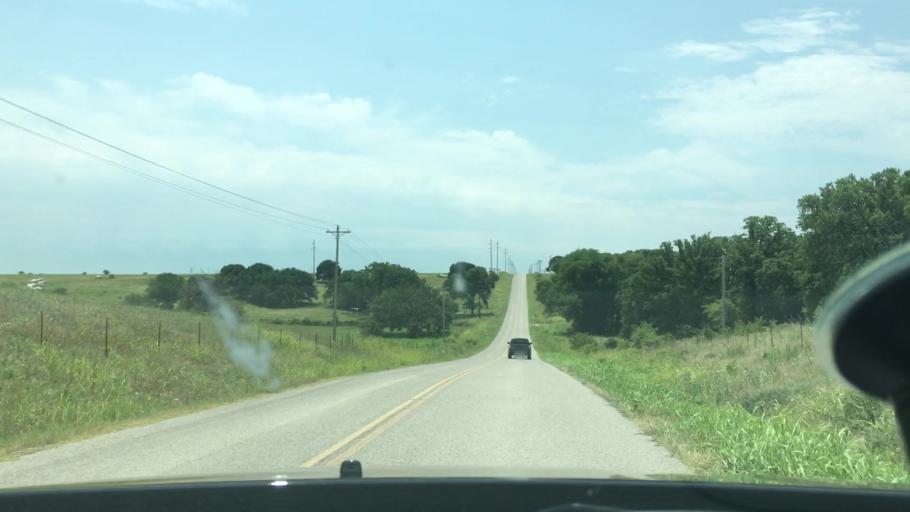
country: US
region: Oklahoma
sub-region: Love County
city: Marietta
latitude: 33.9280
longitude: -97.3521
